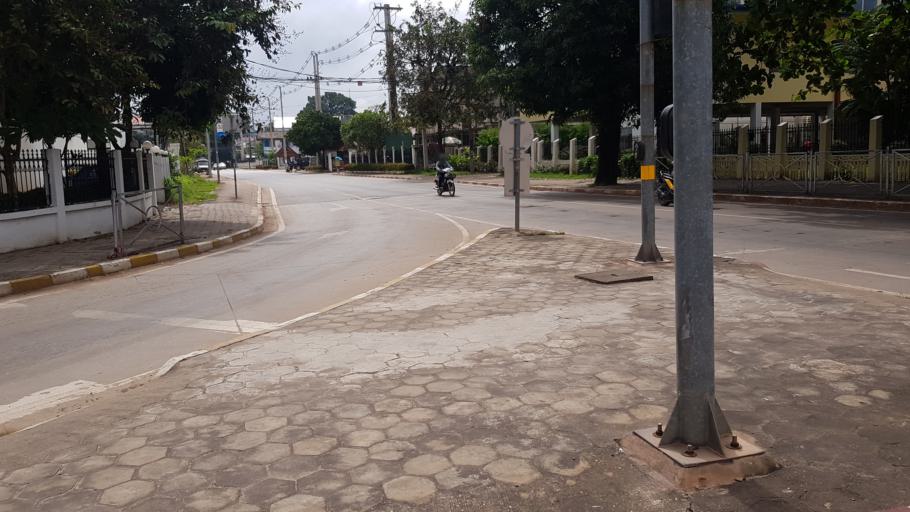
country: LA
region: Vientiane
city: Vientiane
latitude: 17.9644
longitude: 102.6122
